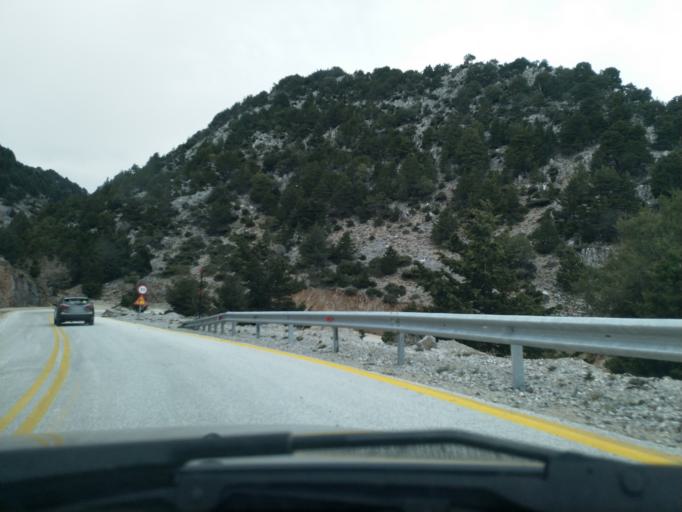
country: GR
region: Crete
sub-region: Nomos Chanias
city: Gerani
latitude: 35.3628
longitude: 23.9104
